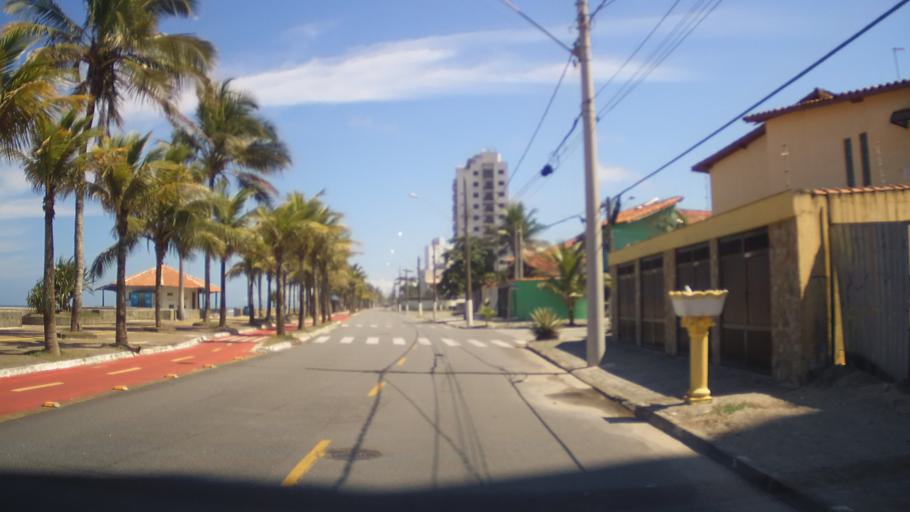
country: BR
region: Sao Paulo
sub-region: Mongagua
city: Mongagua
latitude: -24.1170
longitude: -46.6617
